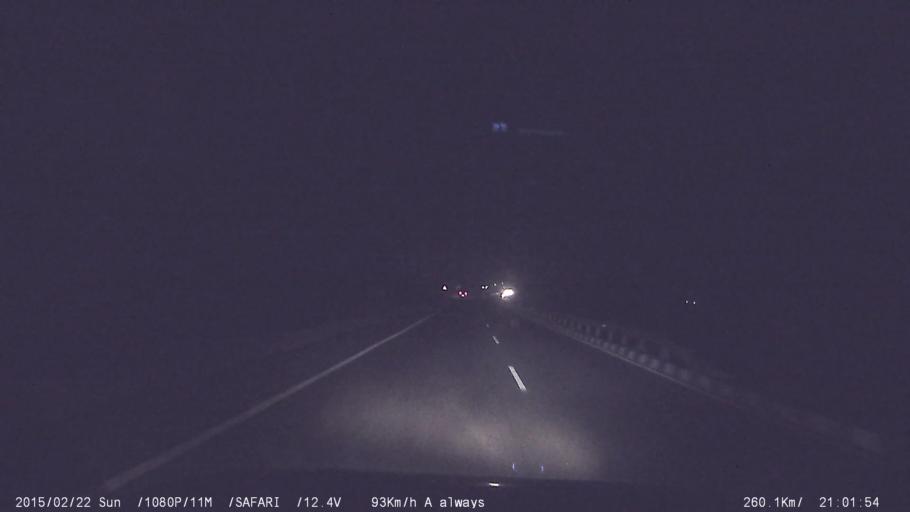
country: IN
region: Tamil Nadu
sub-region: Karur
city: Pallappatti
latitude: 10.6706
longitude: 77.9314
